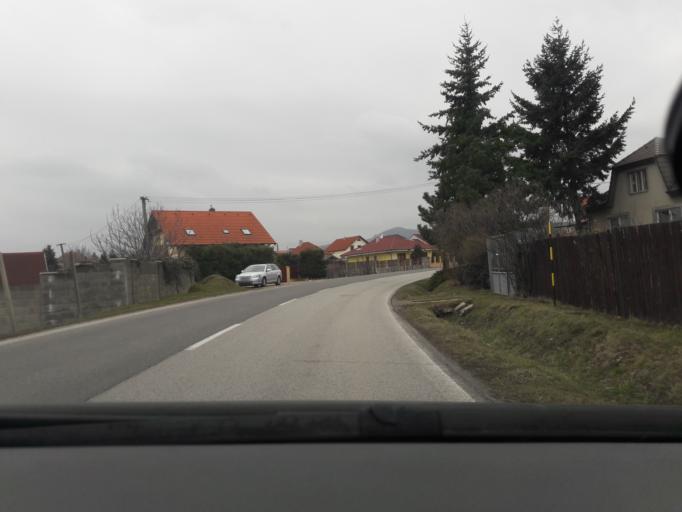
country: SK
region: Bratislavsky
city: Modra
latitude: 48.4011
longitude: 17.3688
